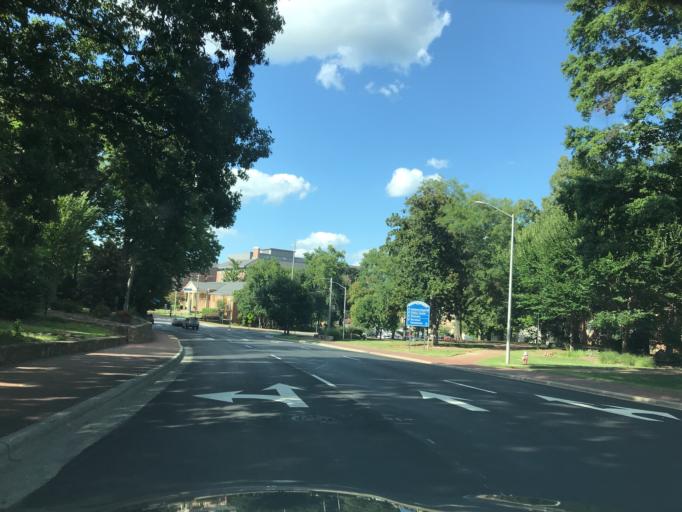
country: US
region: North Carolina
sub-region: Orange County
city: Chapel Hill
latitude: 35.9076
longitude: -79.0529
